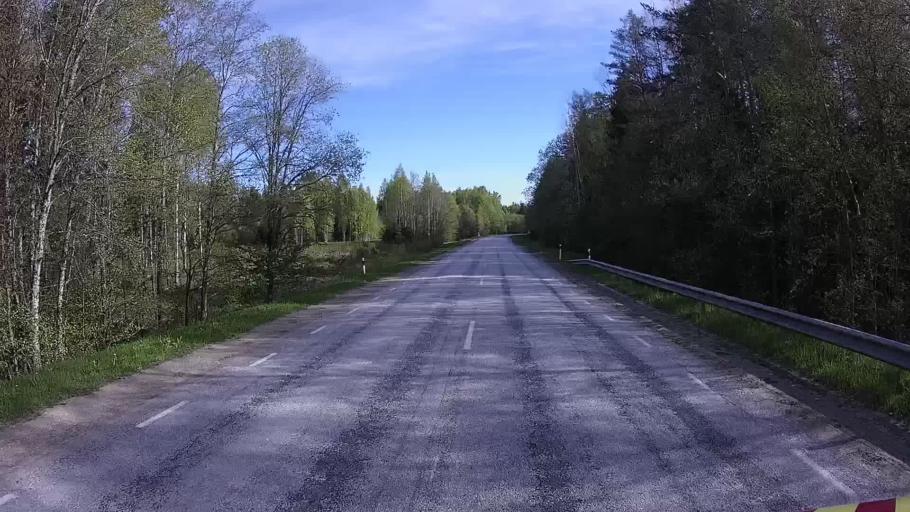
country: EE
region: Tartu
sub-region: Elva linn
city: Elva
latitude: 58.0995
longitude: 26.4939
